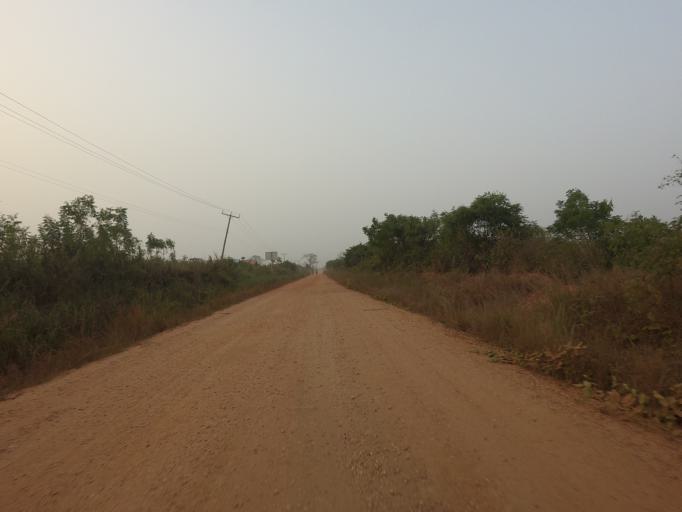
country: GH
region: Volta
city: Anloga
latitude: 5.9749
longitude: 0.6081
